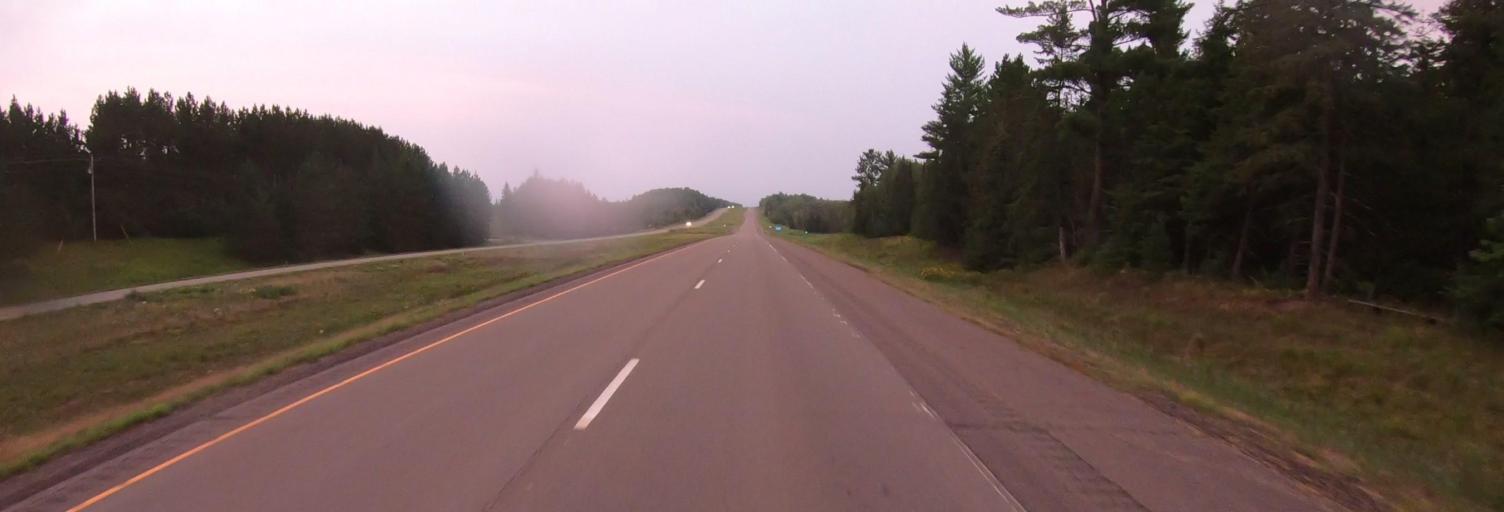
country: US
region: Minnesota
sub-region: Carlton County
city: Cloquet
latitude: 46.9922
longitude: -92.4708
